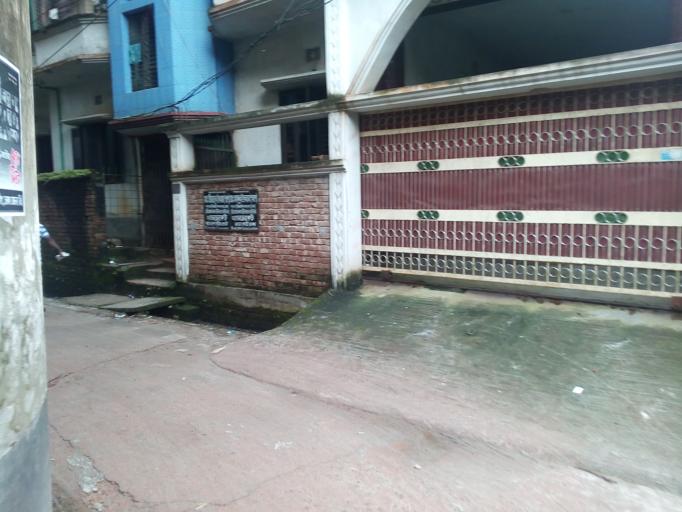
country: BD
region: Dhaka
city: Tungi
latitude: 23.8433
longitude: 90.2494
